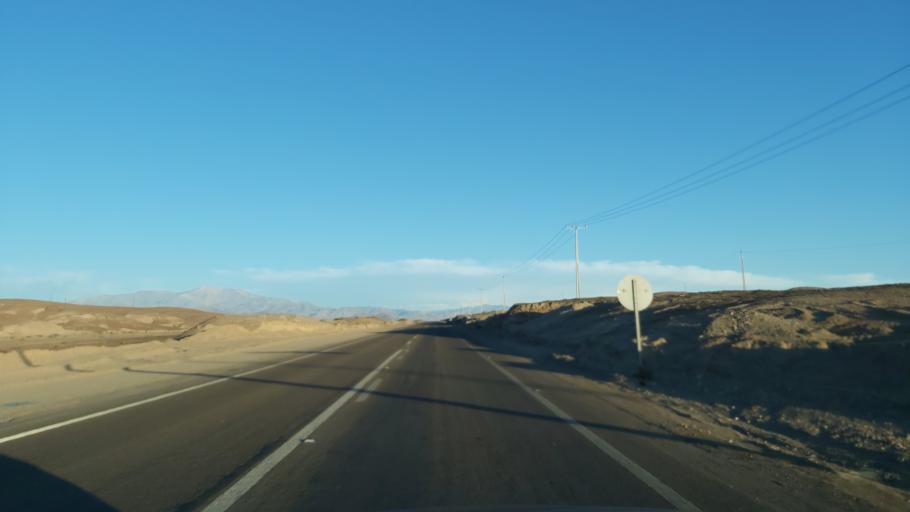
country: CL
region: Atacama
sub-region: Provincia de Chanaral
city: Diego de Almagro
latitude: -26.4273
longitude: -70.0160
